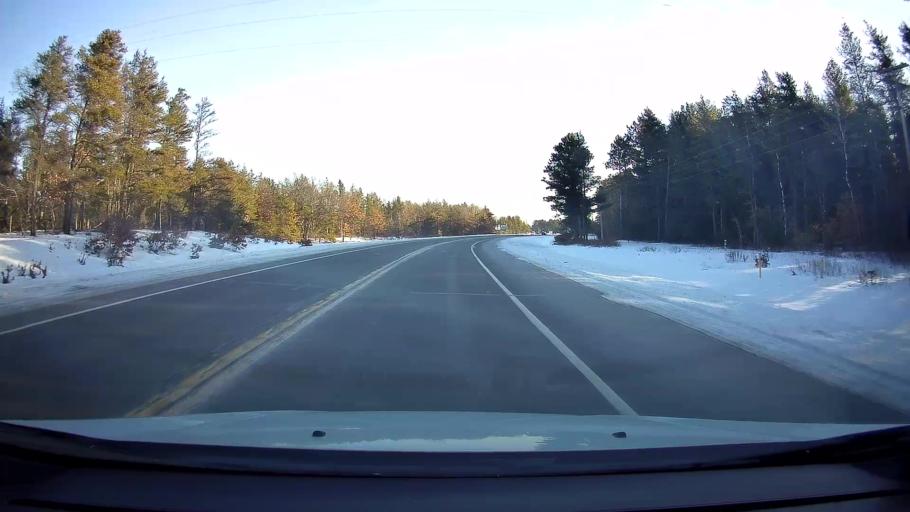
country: US
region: Wisconsin
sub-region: Washburn County
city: Spooner
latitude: 45.9099
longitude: -91.8056
